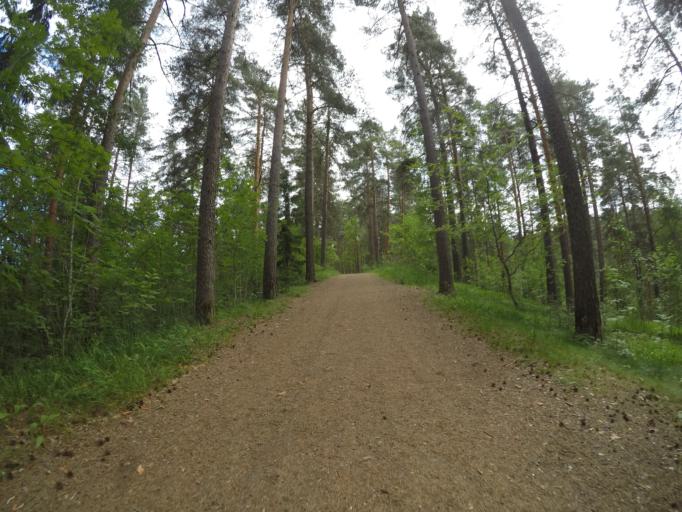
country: FI
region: Haeme
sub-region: Haemeenlinna
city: Haemeenlinna
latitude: 60.9926
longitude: 24.4236
